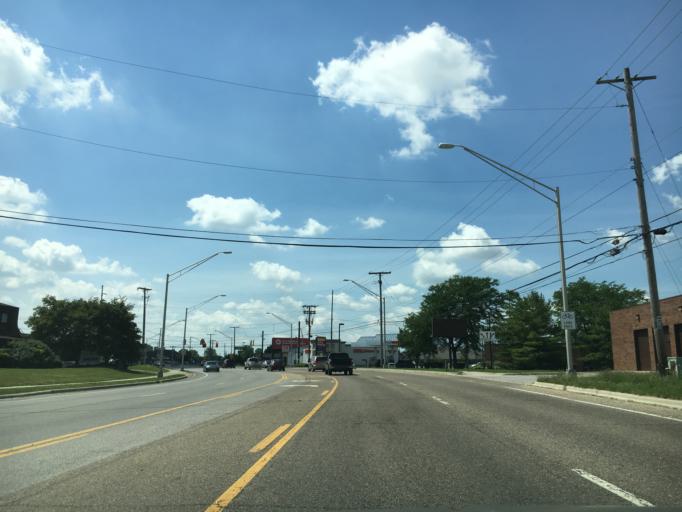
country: US
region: Ohio
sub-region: Franklin County
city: Lincoln Village
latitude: 39.9325
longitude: -83.1450
